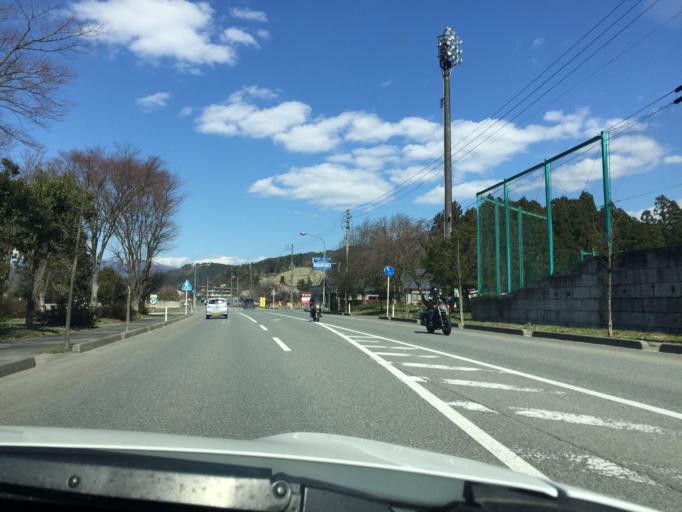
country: JP
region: Yamagata
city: Nagai
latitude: 38.1618
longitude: 140.0790
